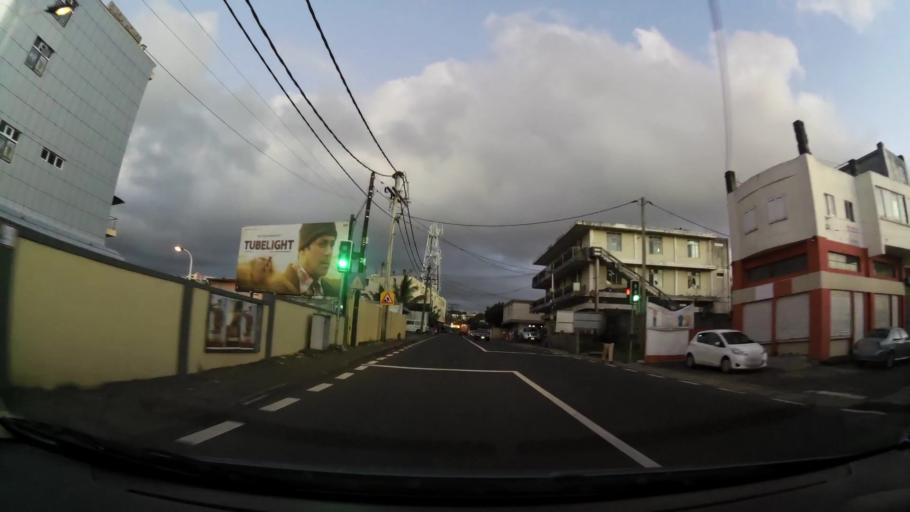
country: MU
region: Plaines Wilhems
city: Curepipe
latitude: -20.2978
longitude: 57.5200
